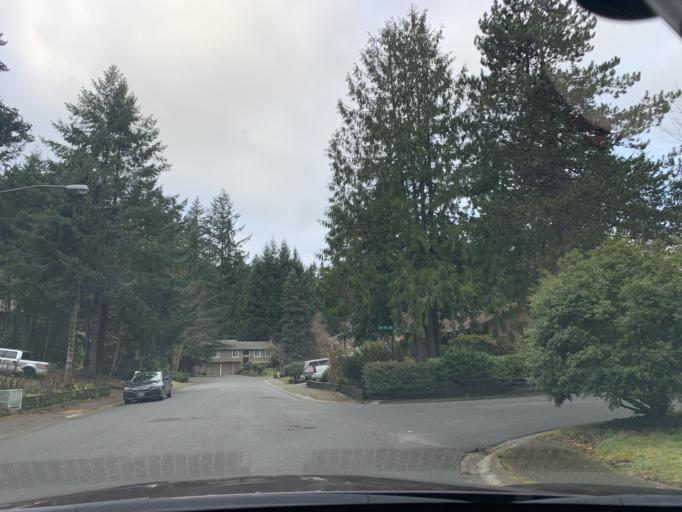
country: US
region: Washington
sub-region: King County
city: Kingsgate
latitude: 47.7351
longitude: -122.1813
